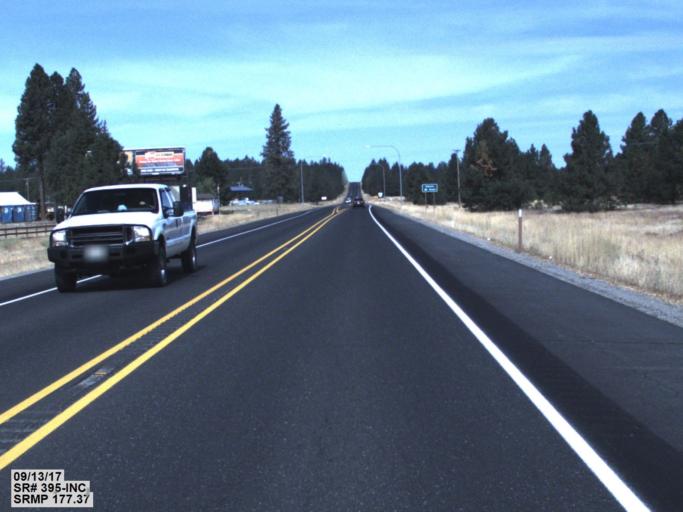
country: US
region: Washington
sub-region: Spokane County
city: Deer Park
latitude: 47.9164
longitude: -117.4521
